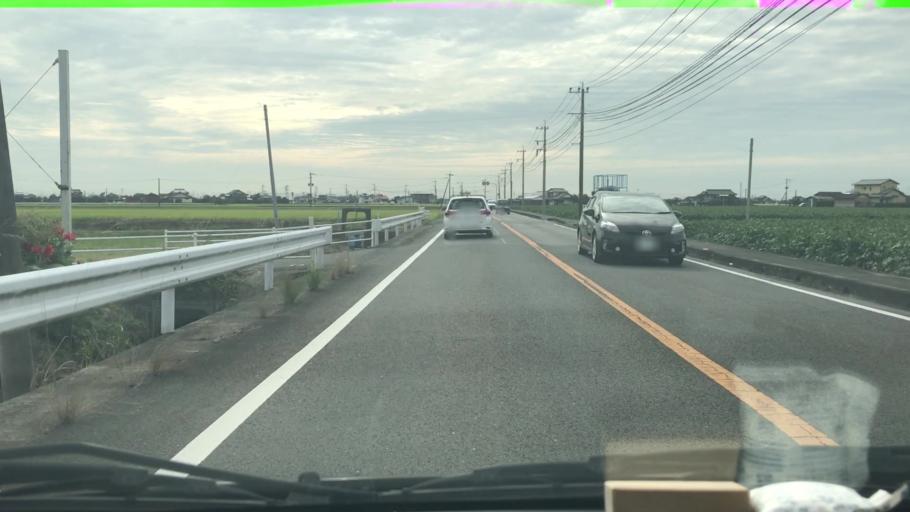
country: JP
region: Saga Prefecture
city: Takeocho-takeo
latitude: 33.2016
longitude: 130.0962
